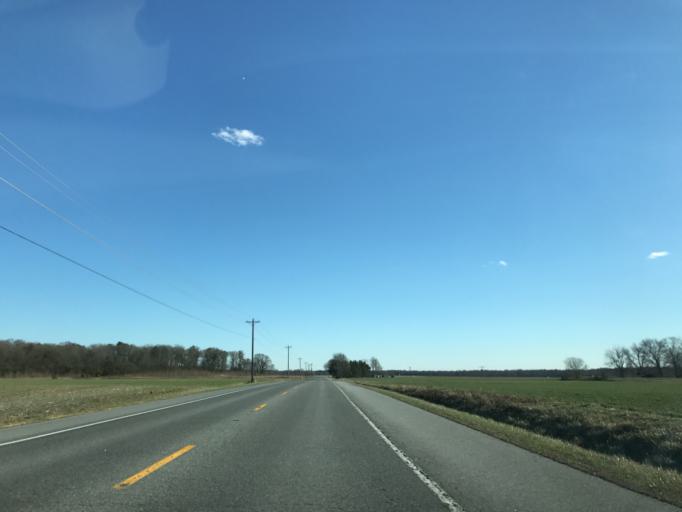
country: US
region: Maryland
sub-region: Caroline County
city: Greensboro
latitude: 39.0764
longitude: -75.8597
